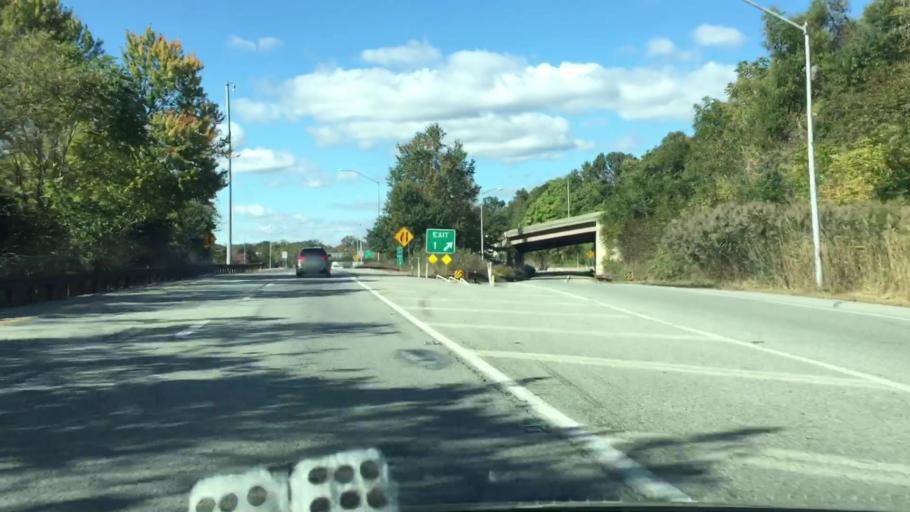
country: US
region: Pennsylvania
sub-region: Delaware County
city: Woodlyn
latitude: 39.8700
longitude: -75.3456
